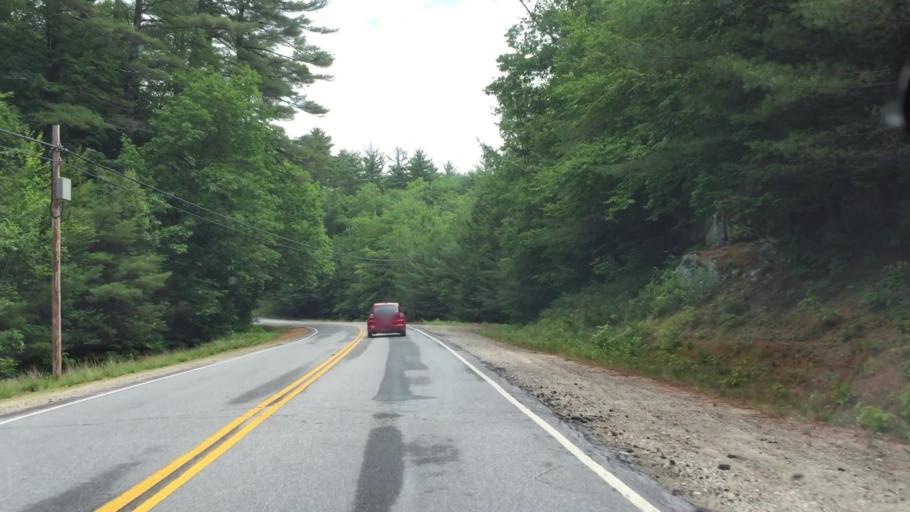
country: US
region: New Hampshire
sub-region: Carroll County
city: Sandwich
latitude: 43.7902
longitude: -71.4582
